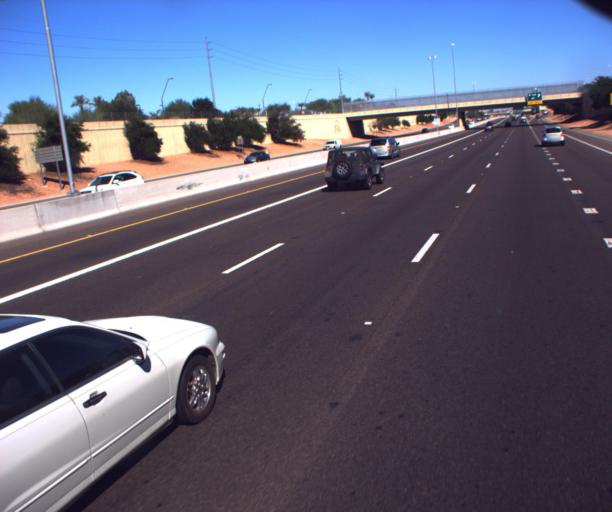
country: US
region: Arizona
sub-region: Maricopa County
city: San Carlos
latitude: 33.3415
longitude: -111.8932
